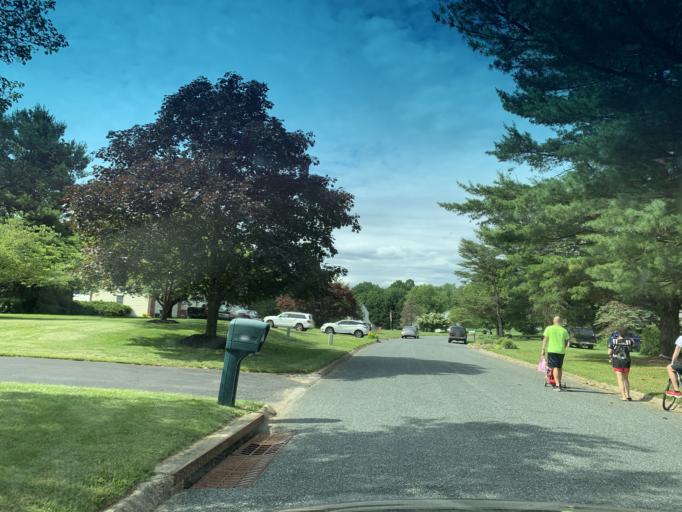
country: US
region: Maryland
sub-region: Harford County
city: Jarrettsville
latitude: 39.5984
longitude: -76.4667
